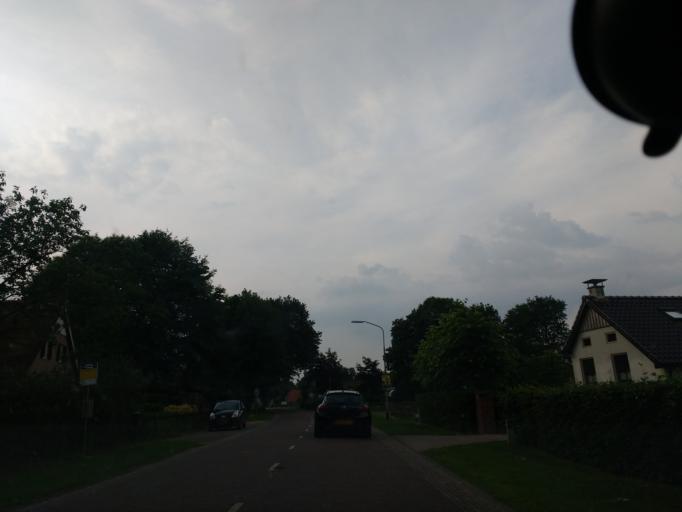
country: NL
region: Drenthe
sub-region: Gemeente Borger-Odoorn
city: Borger
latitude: 52.9007
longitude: 6.8132
